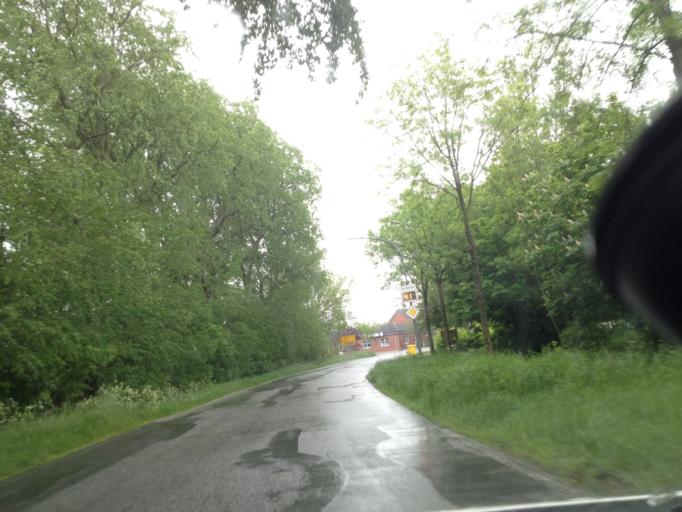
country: DE
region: Schleswig-Holstein
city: Neukirchen
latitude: 54.8746
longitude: 8.7353
